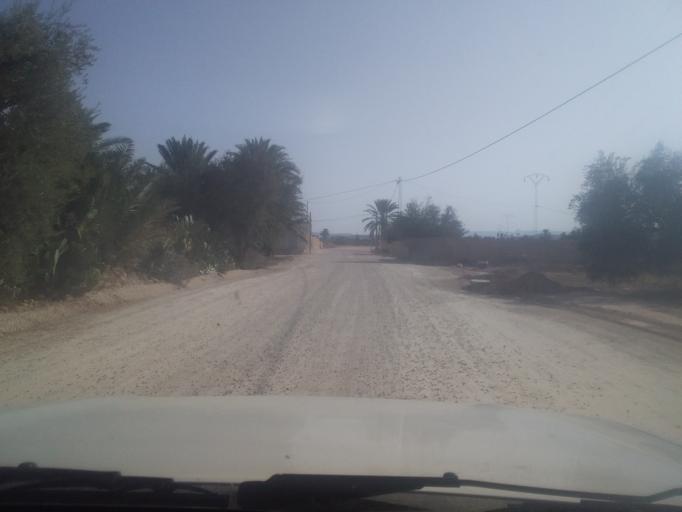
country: TN
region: Qabis
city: Matmata
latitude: 33.6005
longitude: 10.2758
